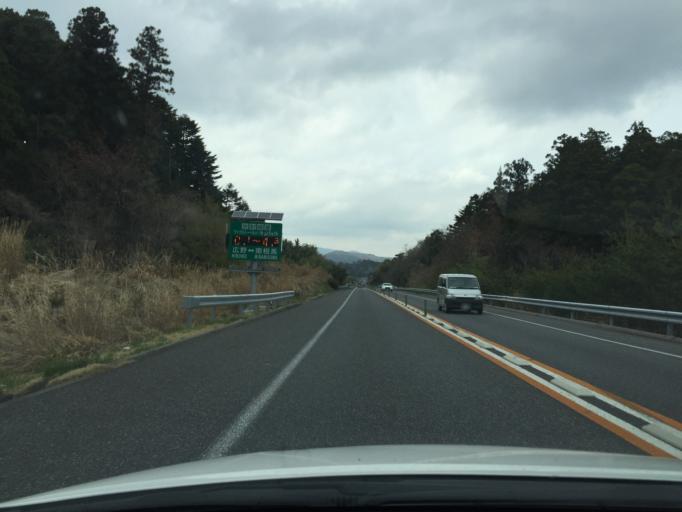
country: JP
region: Fukushima
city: Iwaki
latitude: 37.2071
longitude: 140.9831
